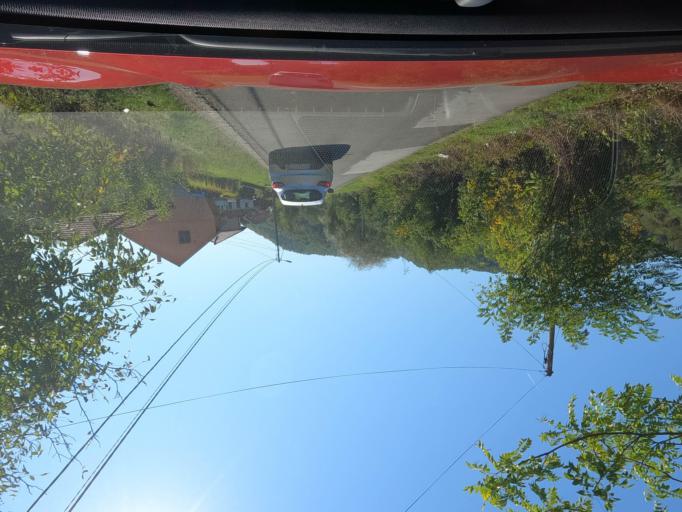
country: RS
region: Central Serbia
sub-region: Raski Okrug
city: Kraljevo
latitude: 43.7391
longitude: 20.7360
